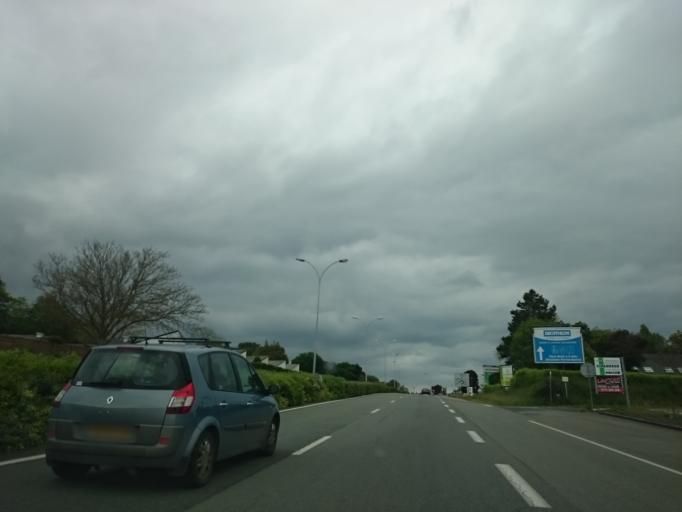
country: FR
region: Brittany
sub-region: Departement des Cotes-d'Armor
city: Lannion
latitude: 48.7441
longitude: -3.4624
